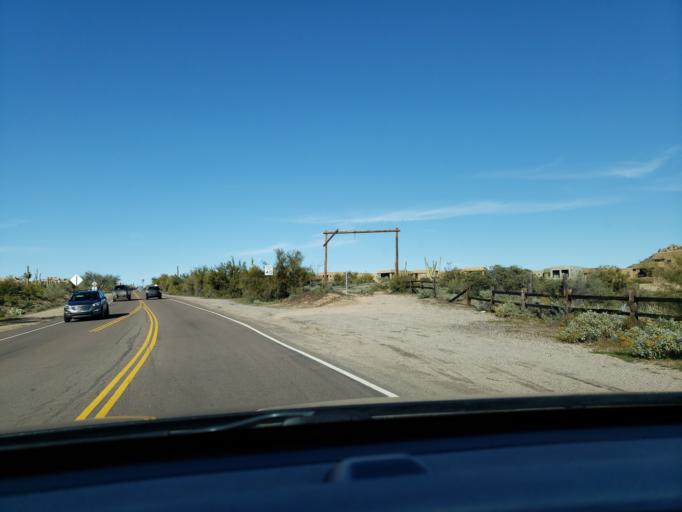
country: US
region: Arizona
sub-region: Maricopa County
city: Carefree
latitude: 33.7270
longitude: -111.8511
